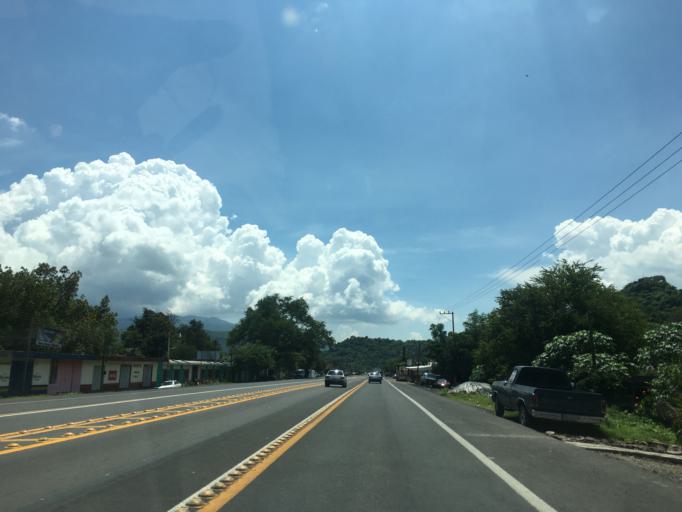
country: MX
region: Nayarit
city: Ixtlan del Rio
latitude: 21.0363
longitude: -104.4108
